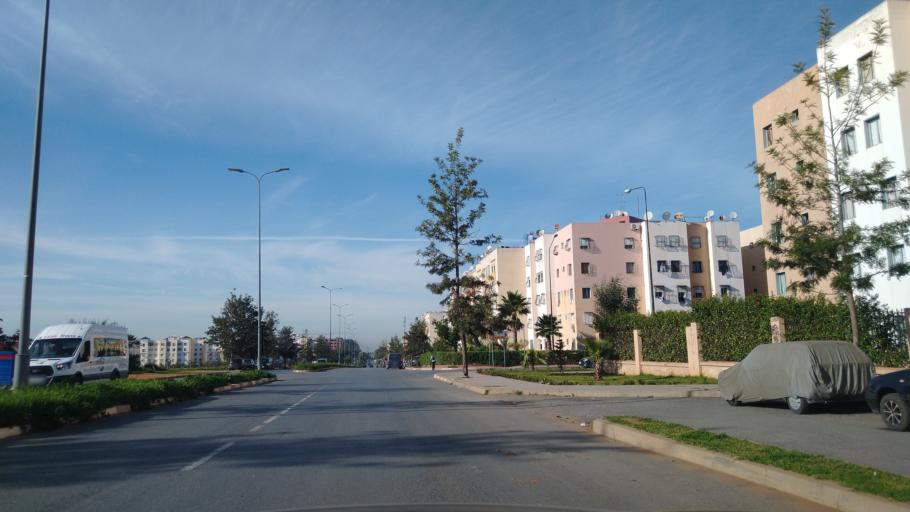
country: MA
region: Rabat-Sale-Zemmour-Zaer
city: Sale
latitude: 33.9906
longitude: -6.7411
